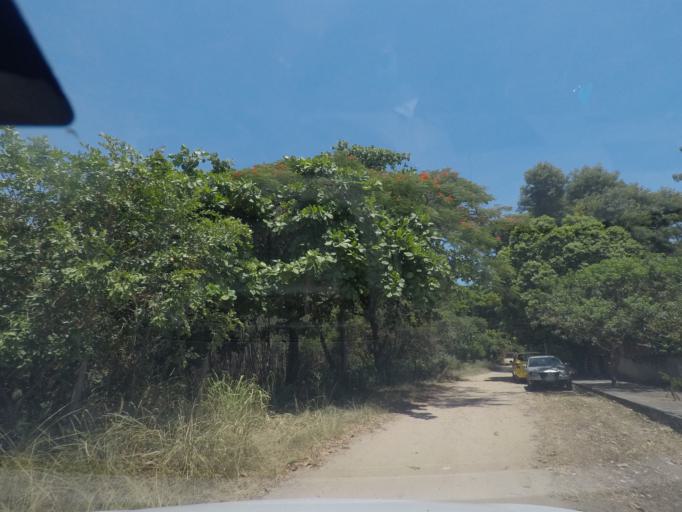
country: BR
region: Rio de Janeiro
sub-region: Niteroi
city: Niteroi
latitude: -22.9664
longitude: -43.0428
